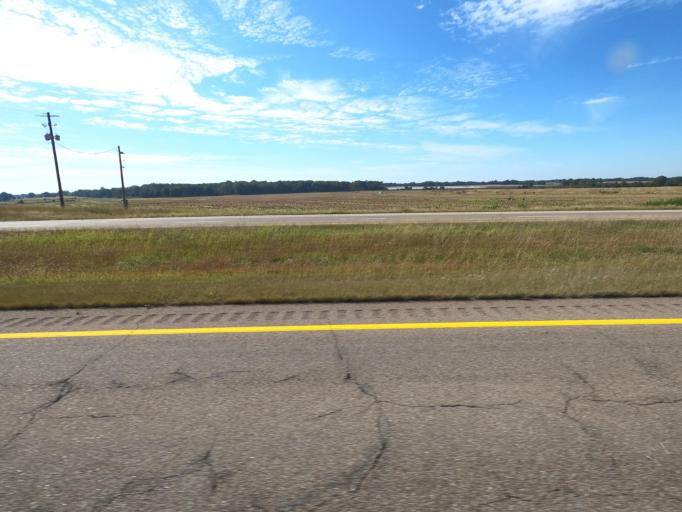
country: US
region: Tennessee
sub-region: Crockett County
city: Alamo
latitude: 35.8273
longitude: -89.1758
